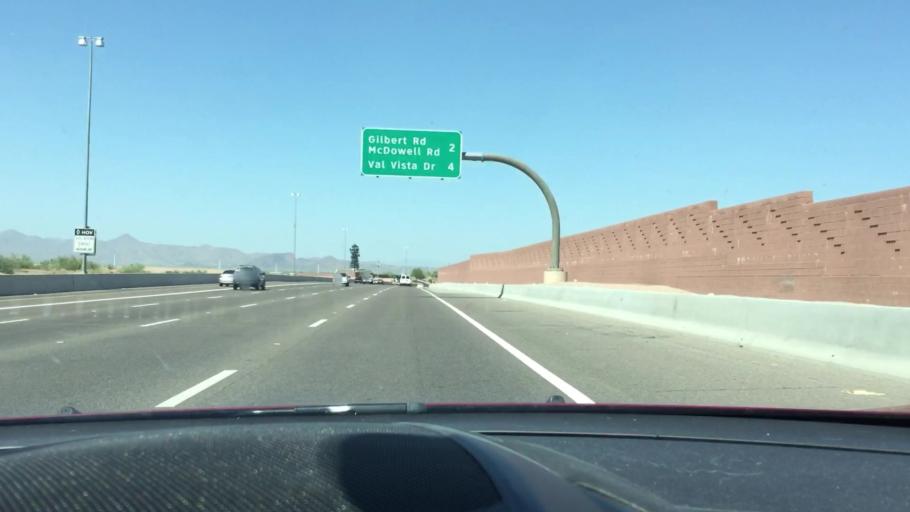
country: US
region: Arizona
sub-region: Maricopa County
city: Mesa
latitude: 33.4611
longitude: -111.8262
